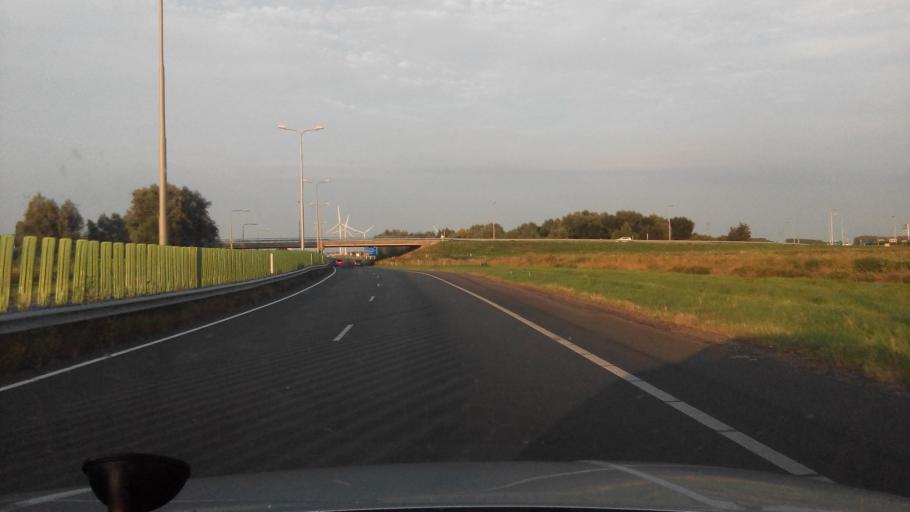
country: NL
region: South Holland
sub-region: Gemeente Rijnwoude
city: Benthuizen
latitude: 52.1220
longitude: 4.5816
